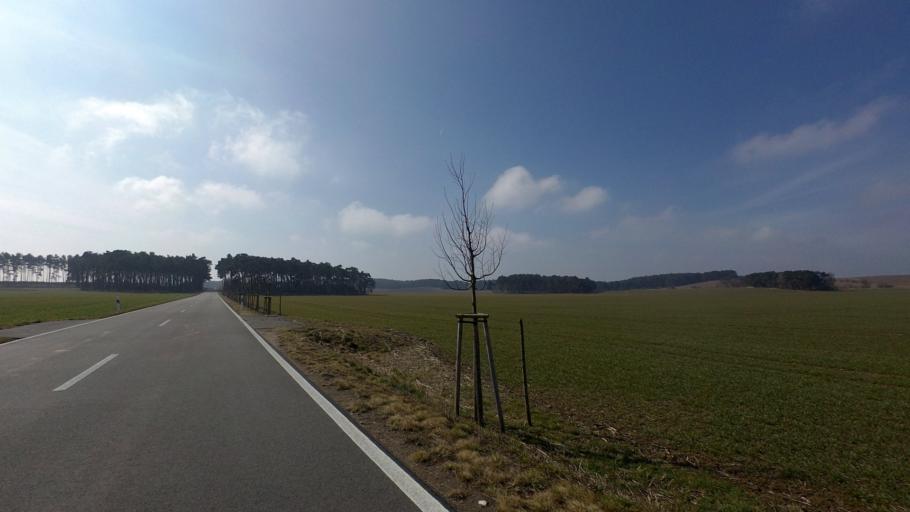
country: DE
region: Brandenburg
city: Belzig
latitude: 52.1233
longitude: 12.6301
